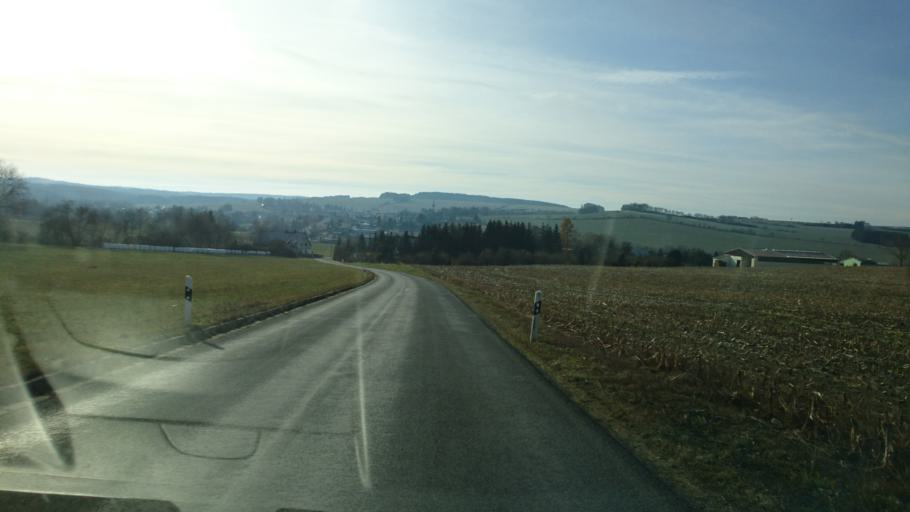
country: DE
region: Thuringia
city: Tanna
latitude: 50.5072
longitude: 11.8656
